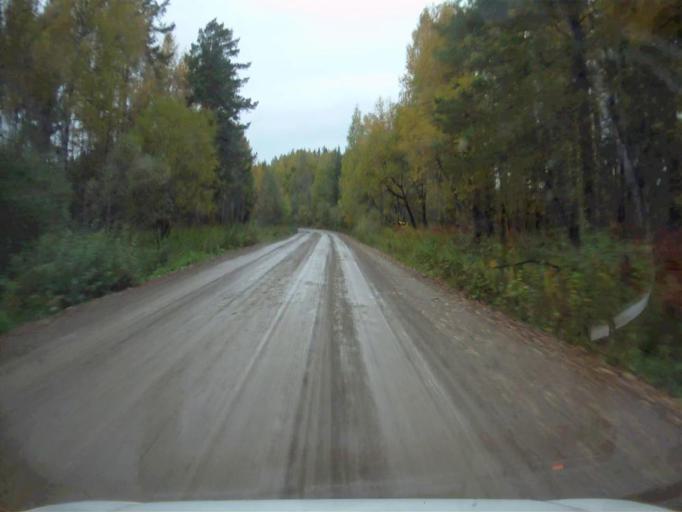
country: RU
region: Chelyabinsk
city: Nyazepetrovsk
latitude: 56.1035
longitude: 59.3862
